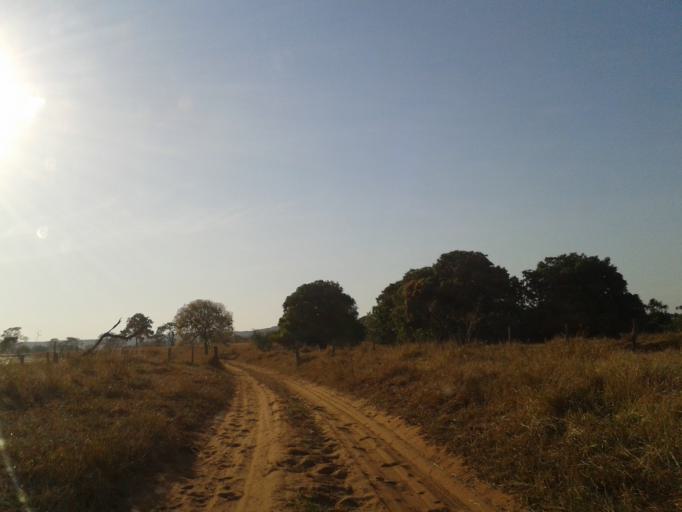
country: BR
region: Minas Gerais
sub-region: Santa Vitoria
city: Santa Vitoria
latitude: -19.1626
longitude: -50.0163
